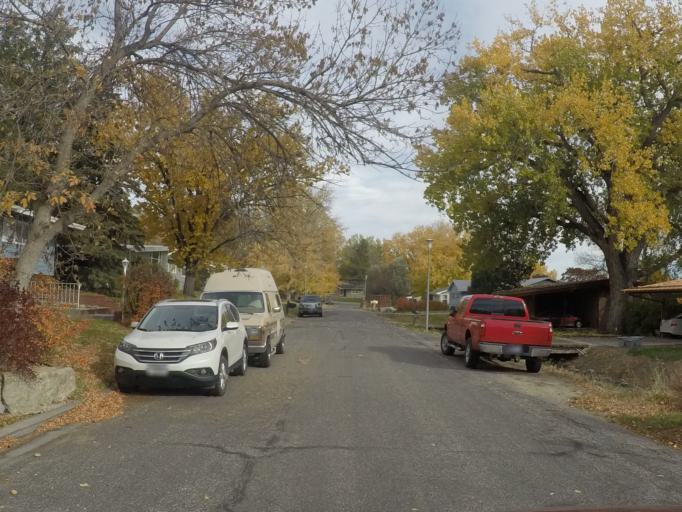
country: US
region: Montana
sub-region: Yellowstone County
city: Billings
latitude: 45.8002
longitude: -108.5532
